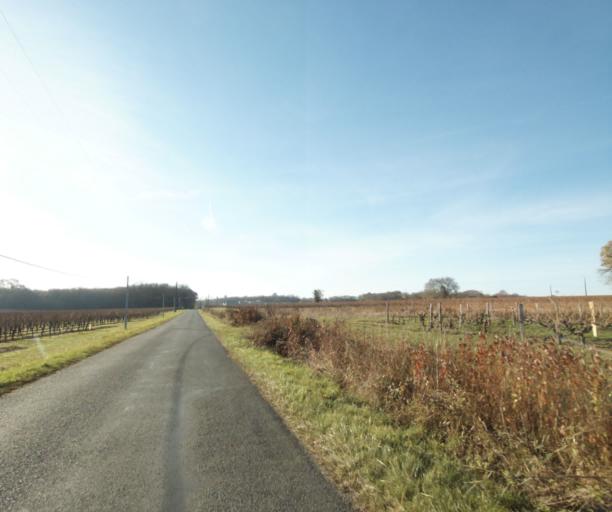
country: FR
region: Poitou-Charentes
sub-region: Departement de la Charente-Maritime
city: Cherac
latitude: 45.7348
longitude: -0.4512
